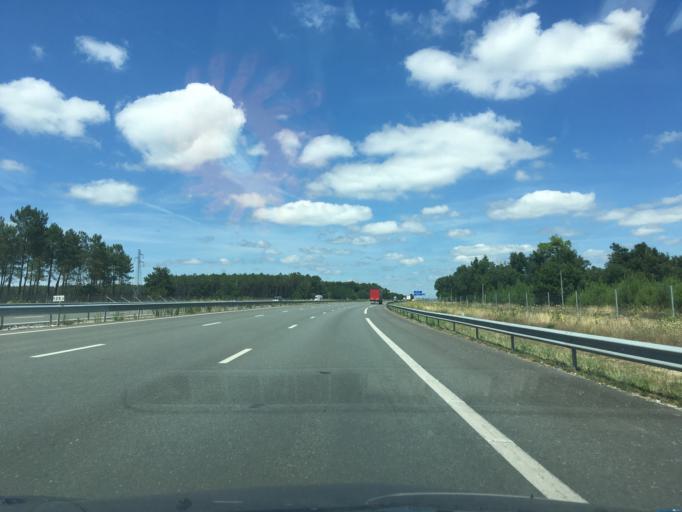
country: FR
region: Aquitaine
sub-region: Departement des Landes
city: Magescq
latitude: 43.7914
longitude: -1.2089
